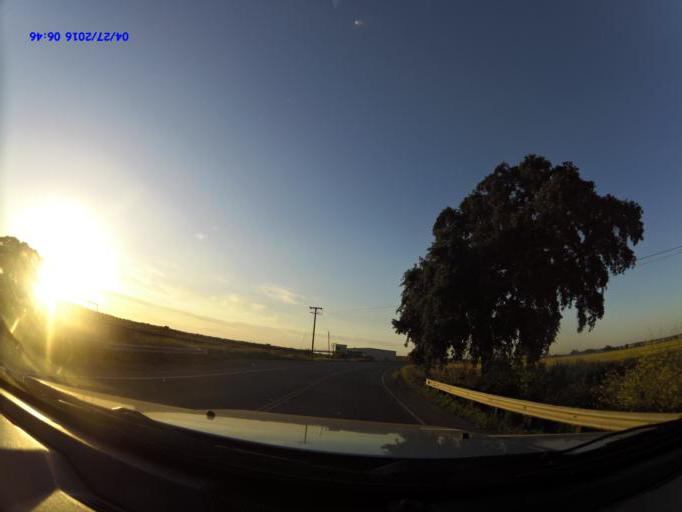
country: US
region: California
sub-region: San Joaquin County
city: Garden Acres
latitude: 37.9159
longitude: -121.1892
